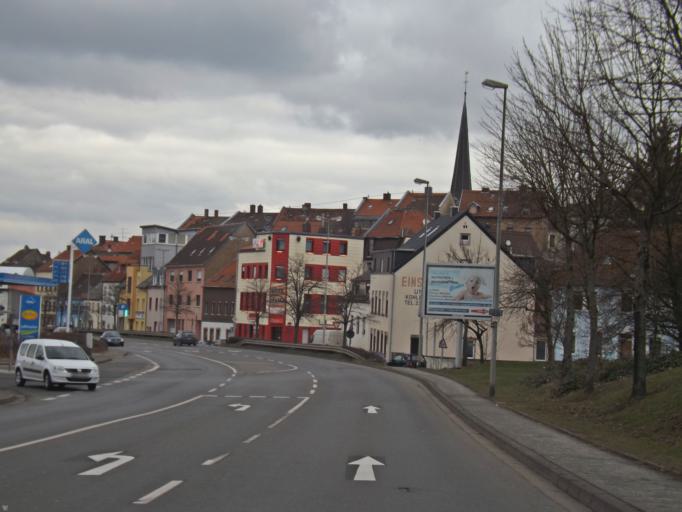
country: DE
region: Saarland
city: Neunkirchen
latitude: 49.3447
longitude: 7.1747
